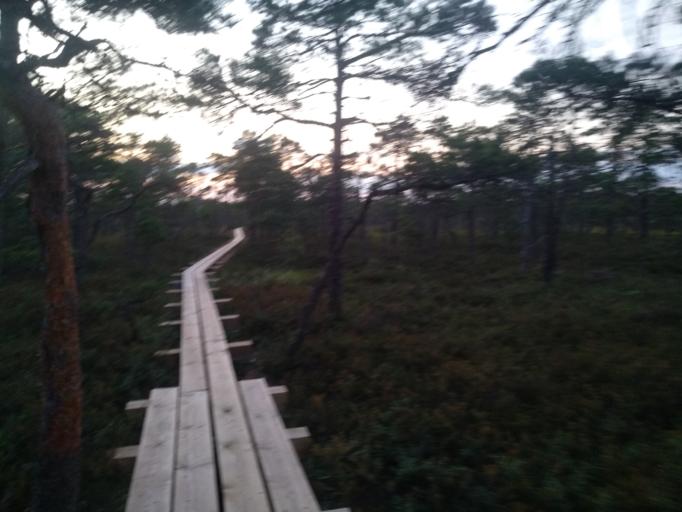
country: EE
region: Jaervamaa
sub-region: Paide linn
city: Paide
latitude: 59.0757
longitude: 25.5235
